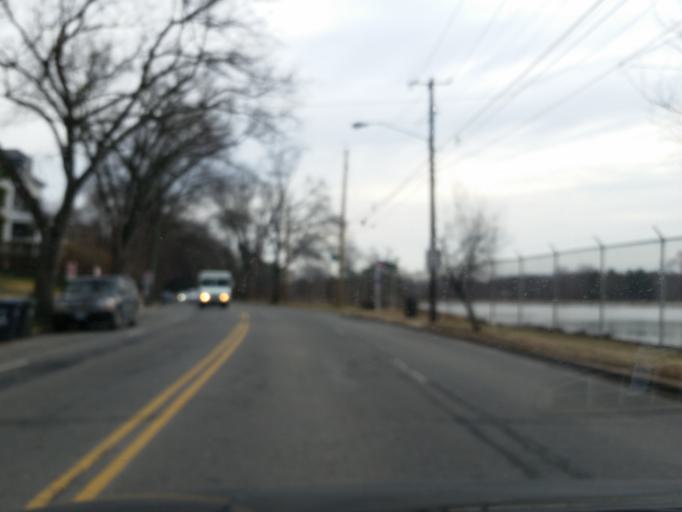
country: US
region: Virginia
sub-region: Arlington County
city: Arlington
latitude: 38.9135
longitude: -77.0919
